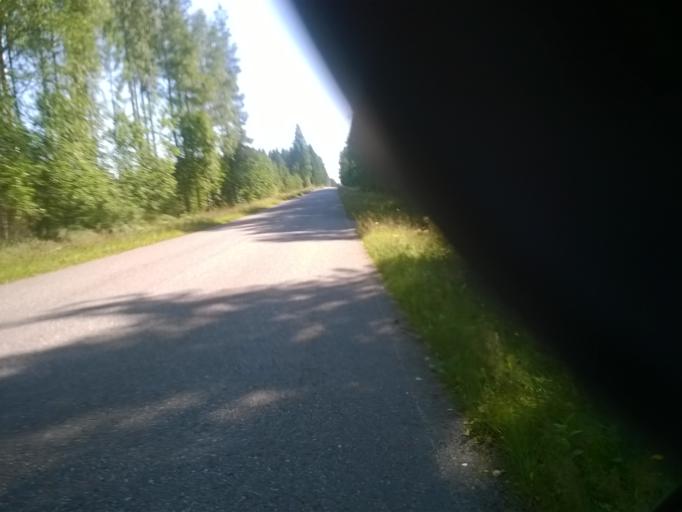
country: FI
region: Kainuu
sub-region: Kehys-Kainuu
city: Kuhmo
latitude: 64.1368
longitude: 29.4219
